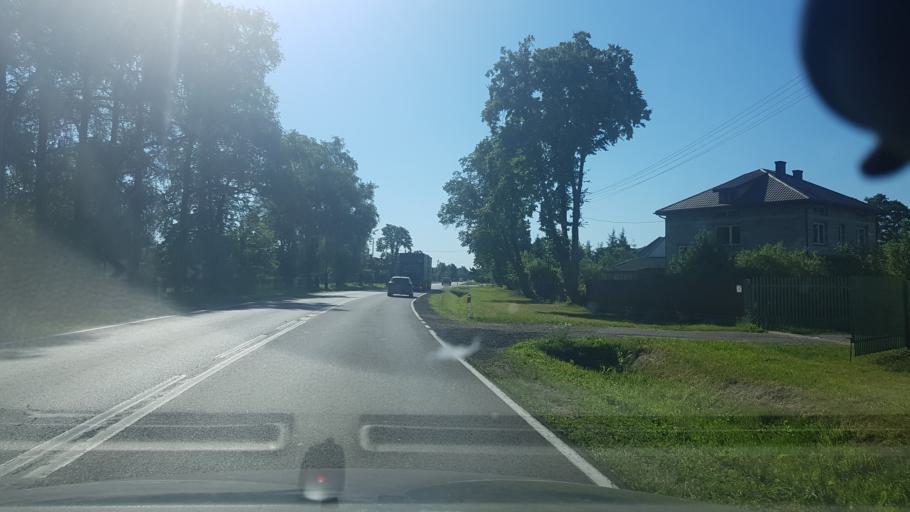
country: PL
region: Masovian Voivodeship
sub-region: Powiat wegrowski
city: Lochow
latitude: 52.5495
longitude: 21.6266
